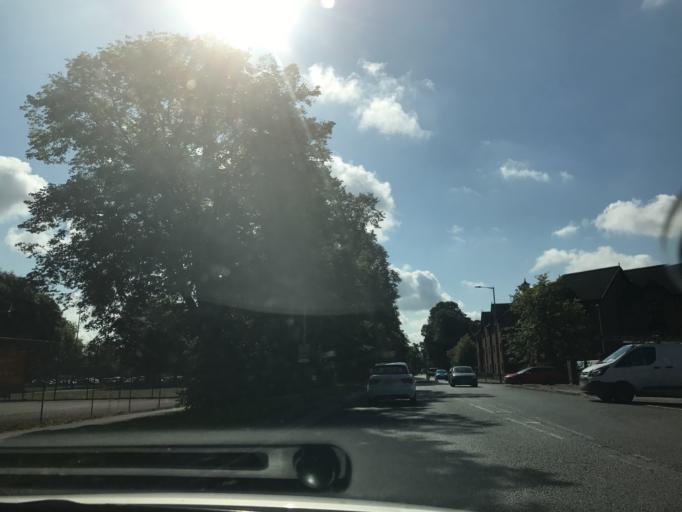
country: GB
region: England
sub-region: Cheshire East
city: Nantwich
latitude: 53.0720
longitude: -2.5163
